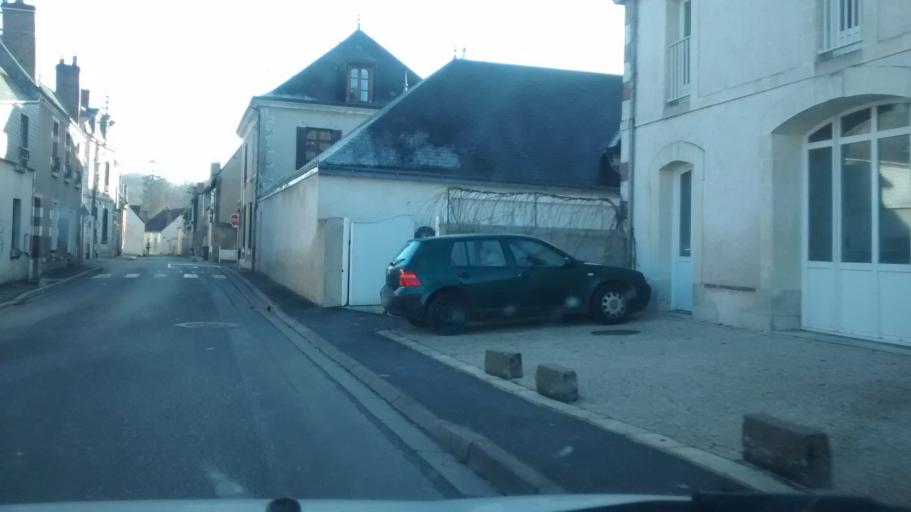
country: FR
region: Centre
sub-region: Departement d'Indre-et-Loire
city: Reugny
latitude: 47.4820
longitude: 0.8835
